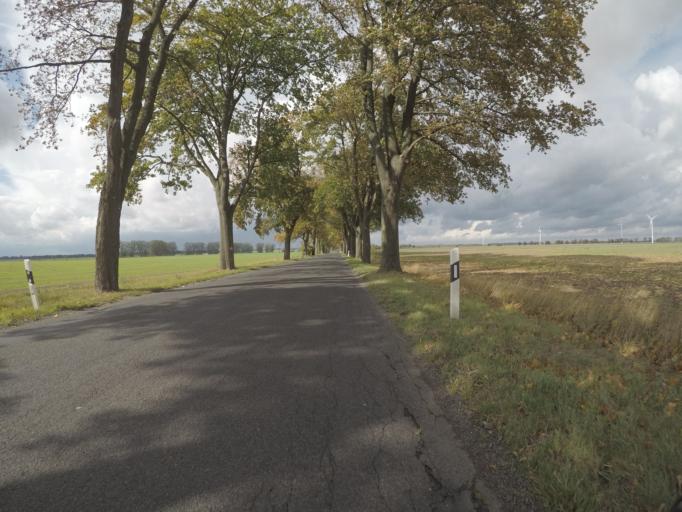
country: DE
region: Brandenburg
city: Altlandsberg
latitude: 52.5918
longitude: 13.7747
